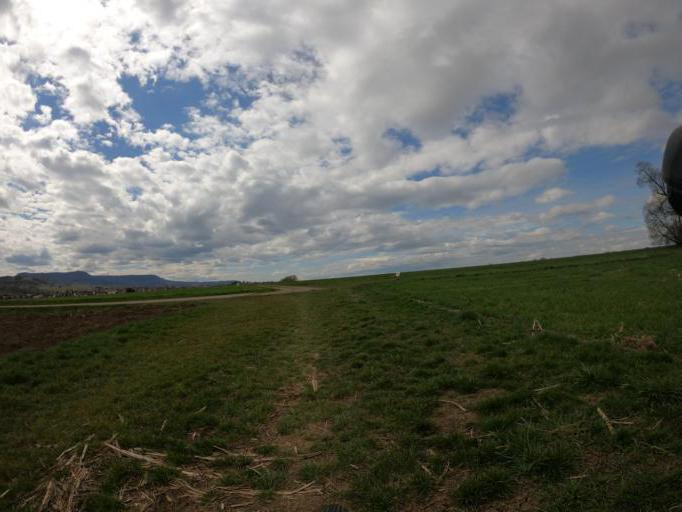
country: DE
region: Baden-Wuerttemberg
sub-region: Tuebingen Region
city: Nehren
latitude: 48.4414
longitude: 9.0727
